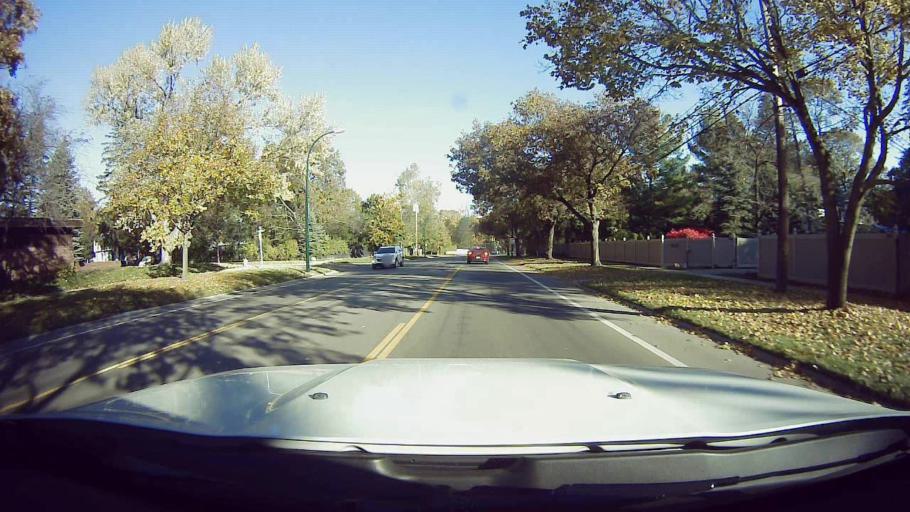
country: US
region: Michigan
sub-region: Oakland County
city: Birmingham
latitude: 42.5462
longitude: -83.2304
